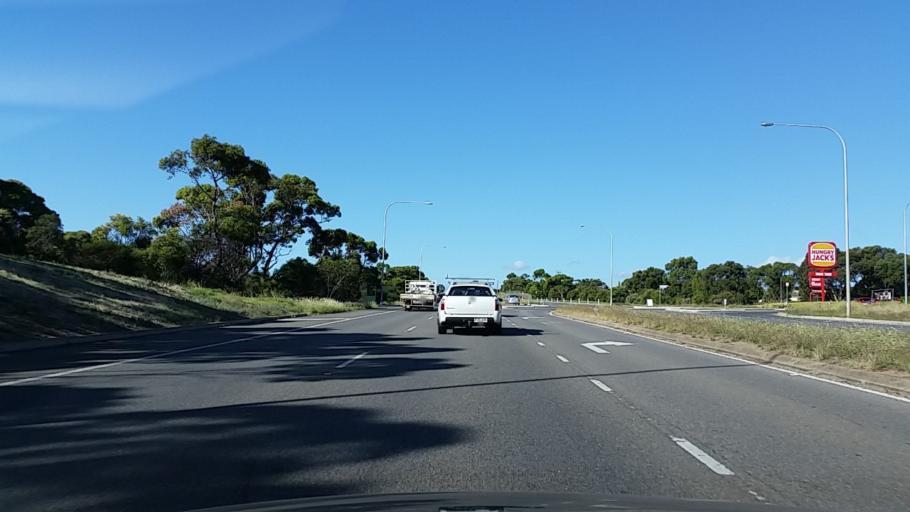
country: AU
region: South Australia
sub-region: Marion
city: Happy Valley
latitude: -35.0756
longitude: 138.5215
